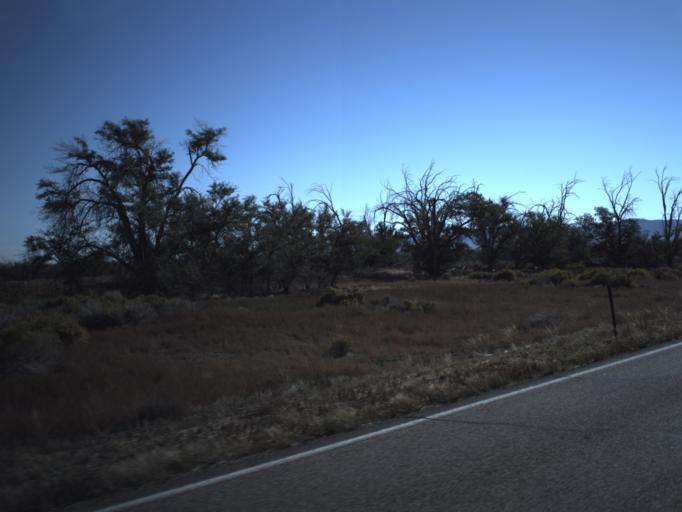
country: US
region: Utah
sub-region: Washington County
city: Enterprise
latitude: 37.7197
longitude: -113.6847
